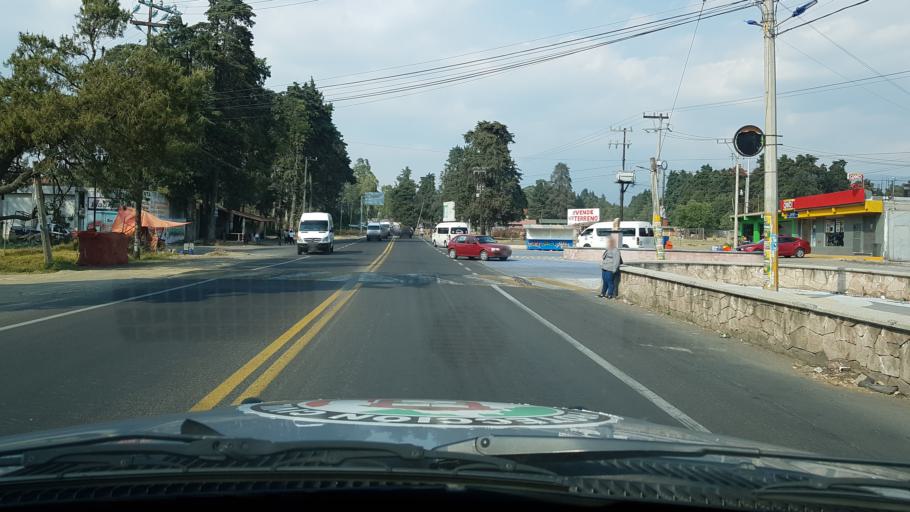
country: MX
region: Mexico
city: Ozumba de Alzate
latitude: 19.0529
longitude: -98.7895
